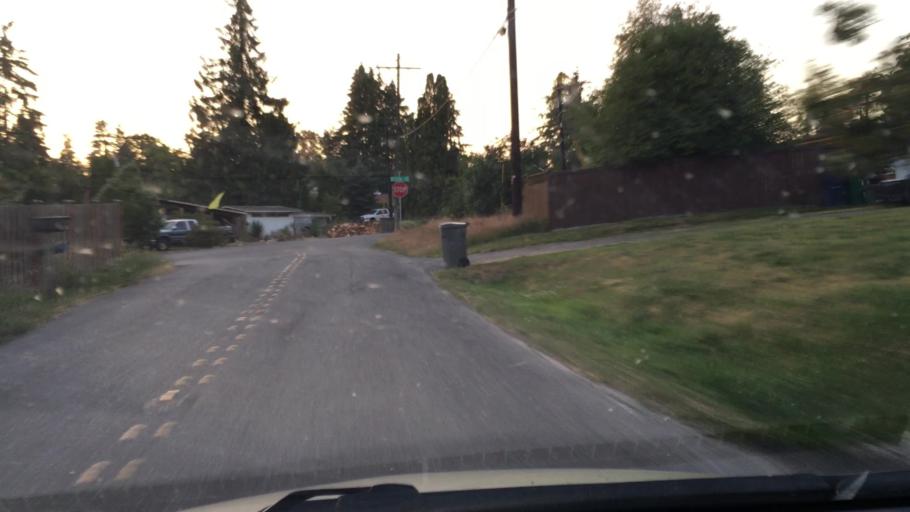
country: US
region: Washington
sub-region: Snohomish County
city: Martha Lake
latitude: 47.8564
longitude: -122.2487
